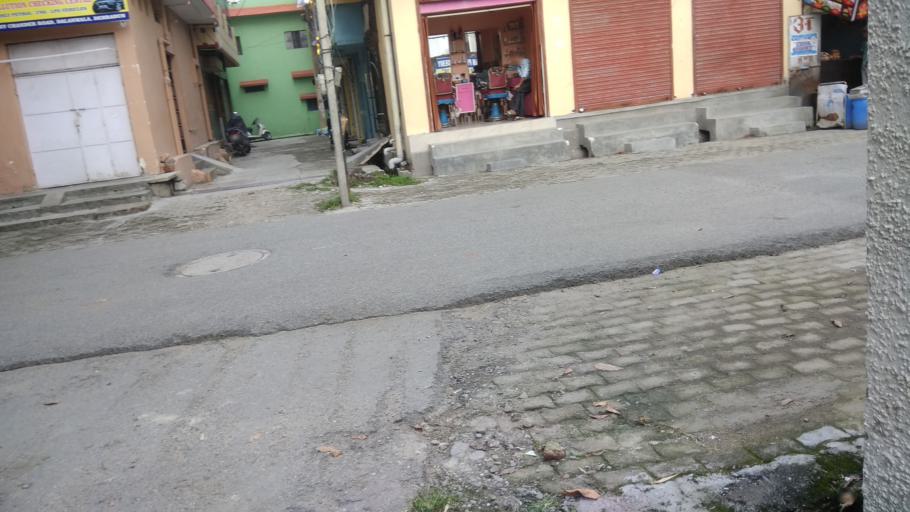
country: IN
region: Uttarakhand
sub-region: Dehradun
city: Raipur
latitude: 30.3126
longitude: 78.0635
